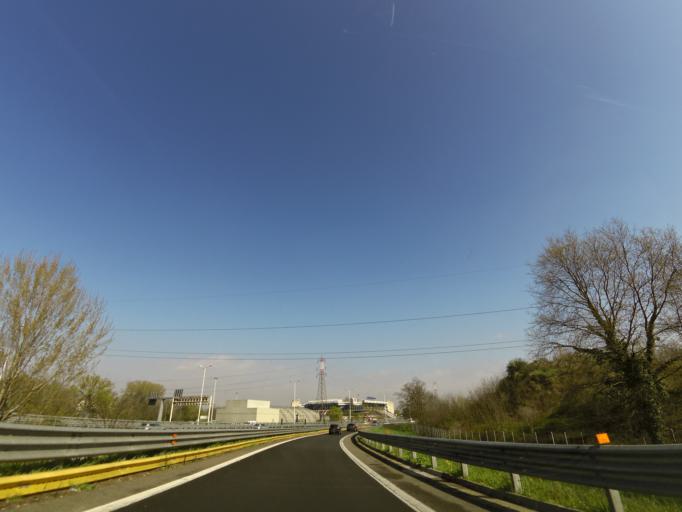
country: IT
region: Lombardy
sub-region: Citta metropolitana di Milano
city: Assago
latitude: 45.3968
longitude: 9.1429
